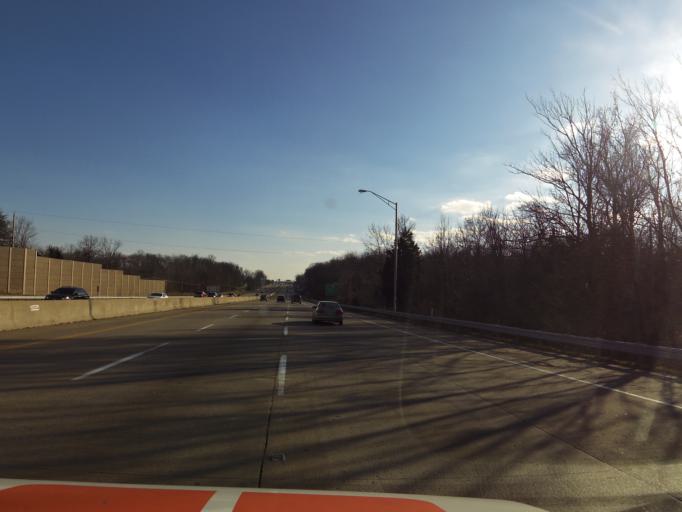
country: US
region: Indiana
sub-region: Clark County
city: Sellersburg
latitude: 38.3875
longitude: -85.7607
